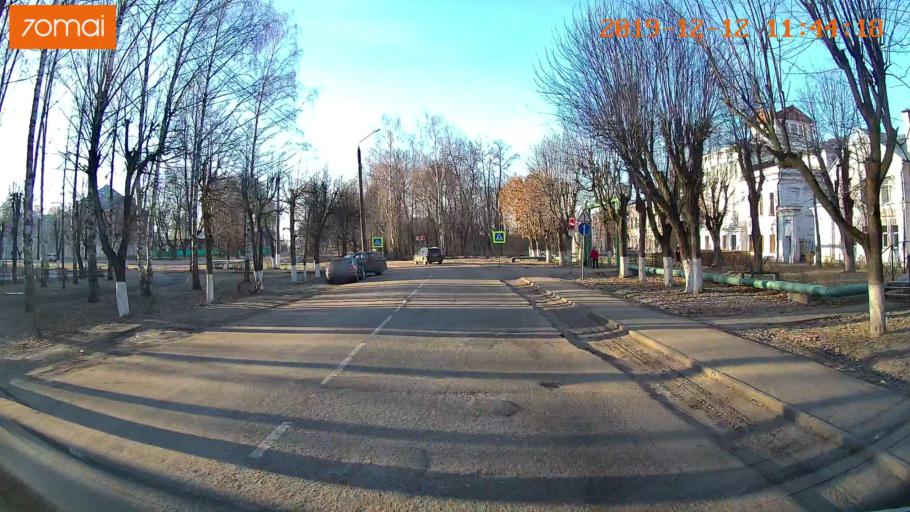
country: RU
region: Ivanovo
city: Shuya
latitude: 56.8554
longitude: 41.3751
